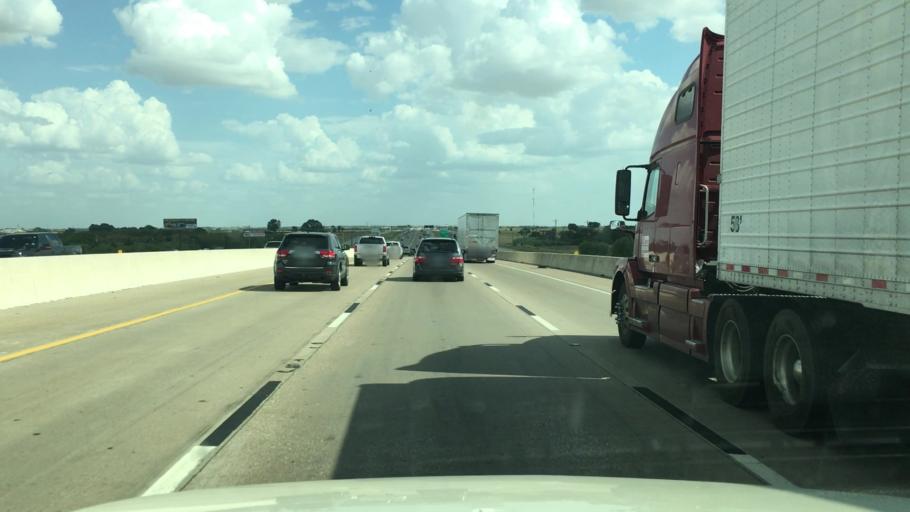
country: US
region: Texas
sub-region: Hill County
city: Hillsboro
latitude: 31.9566
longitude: -97.1152
